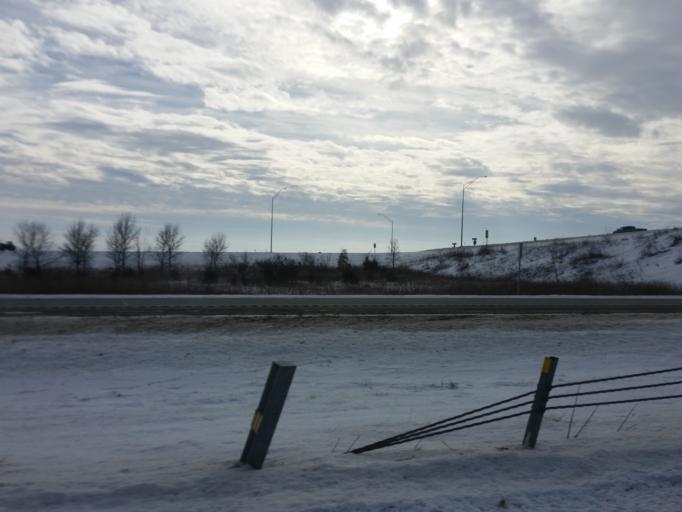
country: US
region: Iowa
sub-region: Buchanan County
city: Independence
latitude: 42.4483
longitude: -91.9185
